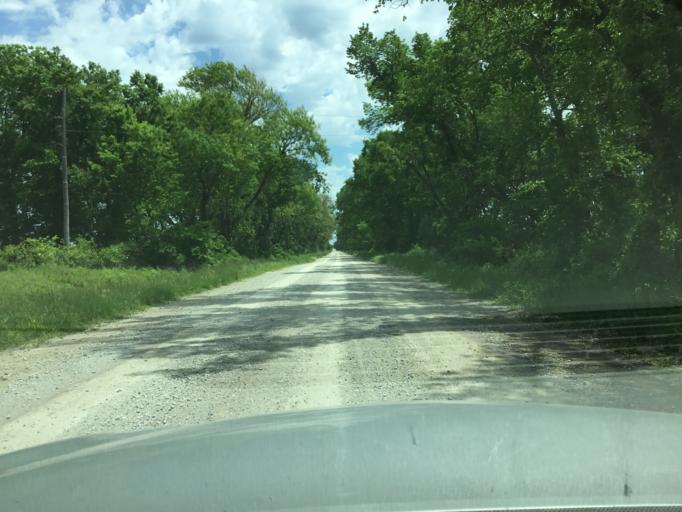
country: US
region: Kansas
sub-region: Montgomery County
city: Independence
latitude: 37.1095
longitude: -95.7745
